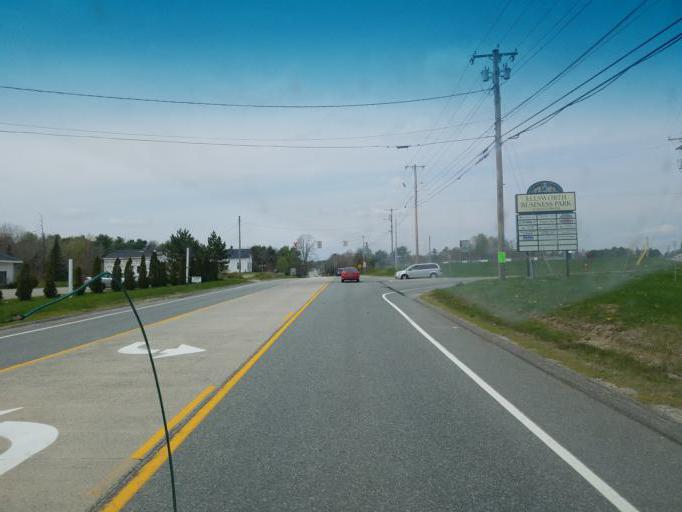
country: US
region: Maine
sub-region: Hancock County
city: Ellsworth
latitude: 44.5688
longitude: -68.4533
